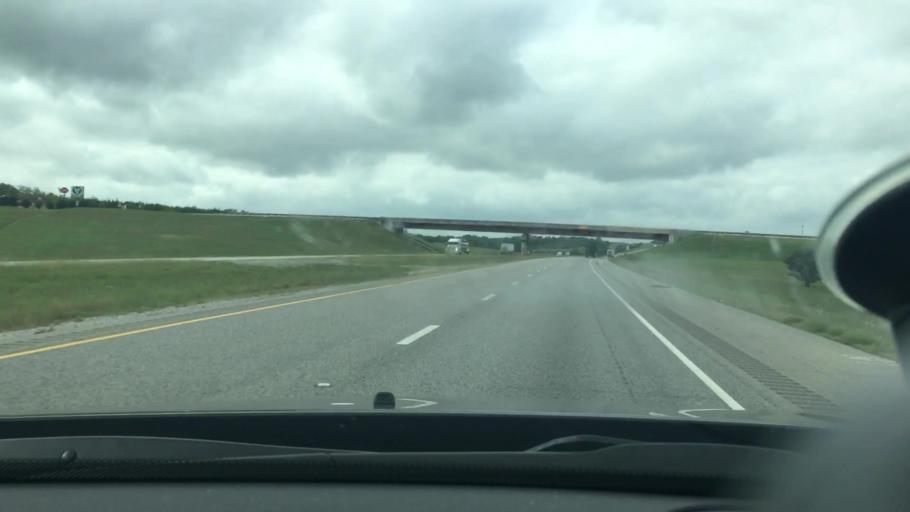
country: US
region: Oklahoma
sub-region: Bryan County
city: Durant
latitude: 34.1339
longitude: -96.2726
